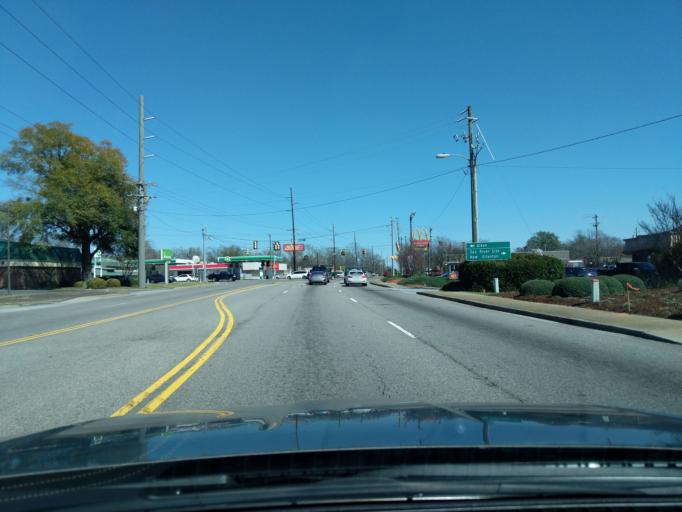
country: US
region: South Carolina
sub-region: Aiken County
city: Aiken
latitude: 33.5233
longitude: -81.7207
